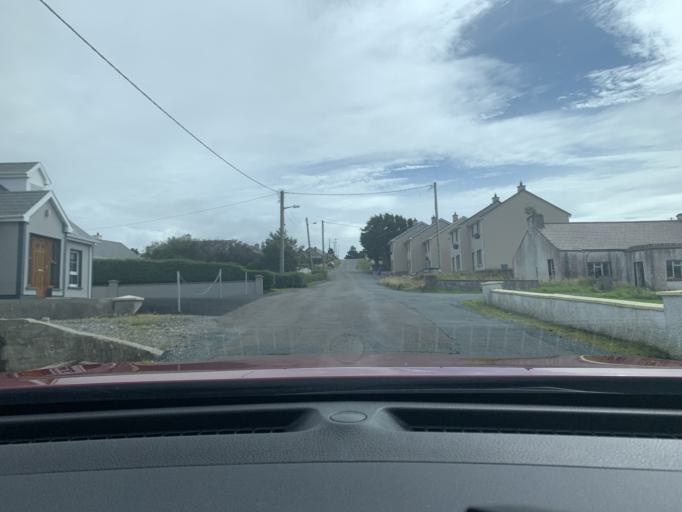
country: IE
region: Ulster
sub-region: County Donegal
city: Dungloe
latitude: 54.9457
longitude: -8.3588
